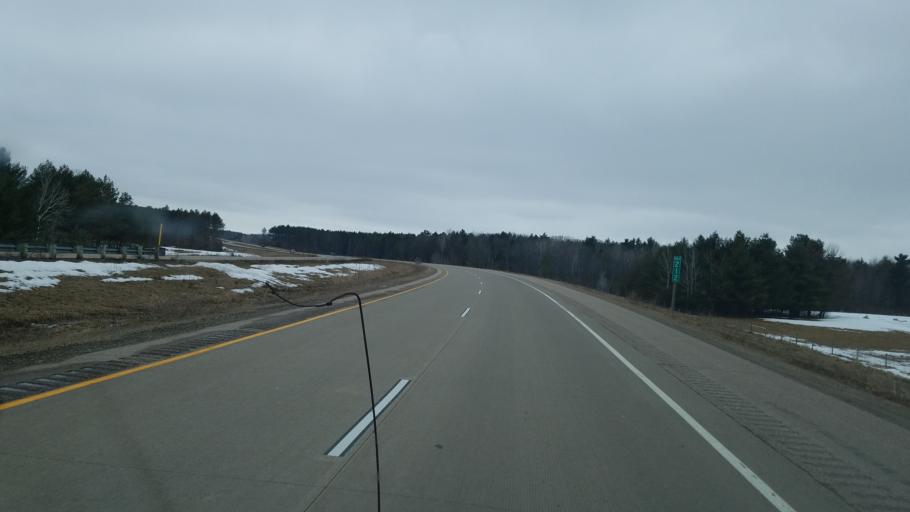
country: US
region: Wisconsin
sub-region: Portage County
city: Stevens Point
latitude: 44.5996
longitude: -89.6482
